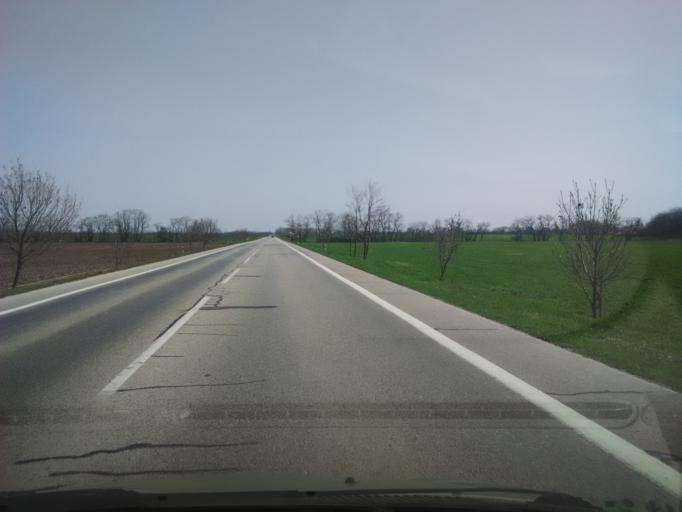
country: SK
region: Nitriansky
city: Sellye
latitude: 48.1450
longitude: 17.9743
